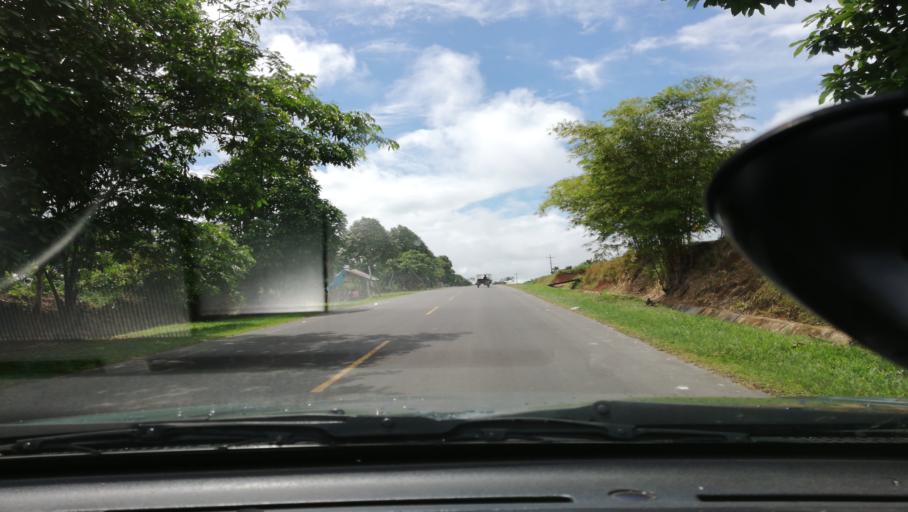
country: PE
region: Loreto
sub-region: Provincia de Maynas
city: Iquitos
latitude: -3.9052
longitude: -73.3585
